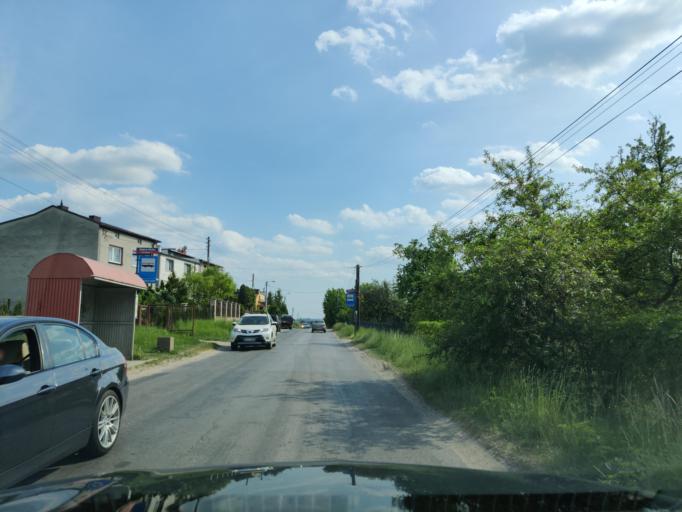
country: PL
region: Silesian Voivodeship
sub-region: Dabrowa Gornicza
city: Dabrowa Gornicza
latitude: 50.3882
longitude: 19.2421
